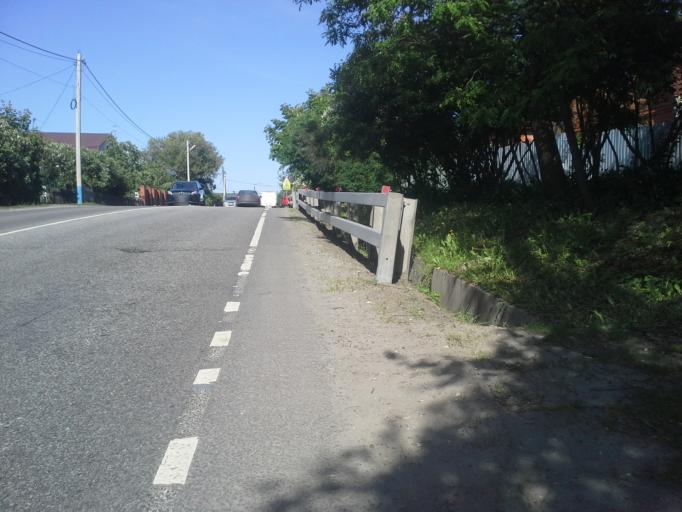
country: RU
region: Moskovskaya
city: Vatutinki
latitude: 55.4332
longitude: 37.3730
